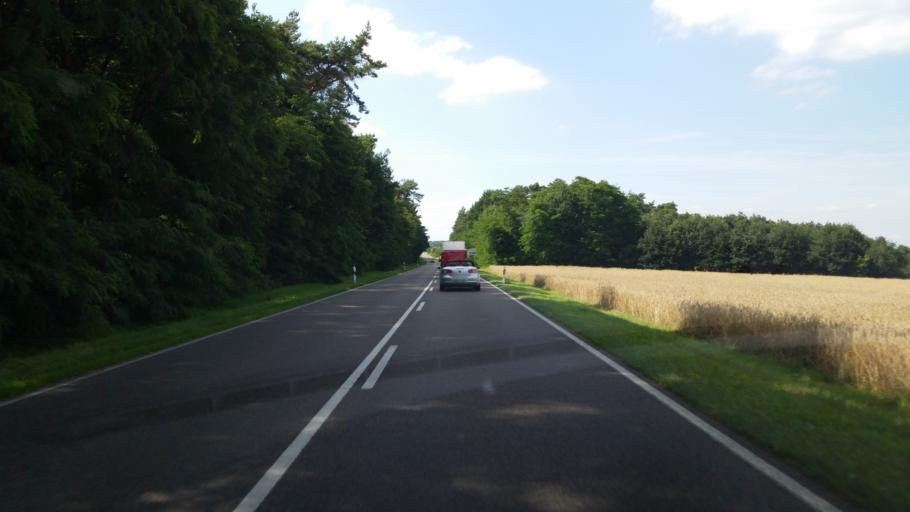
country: DE
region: Saxony
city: Kamenz
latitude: 51.3207
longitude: 14.0862
